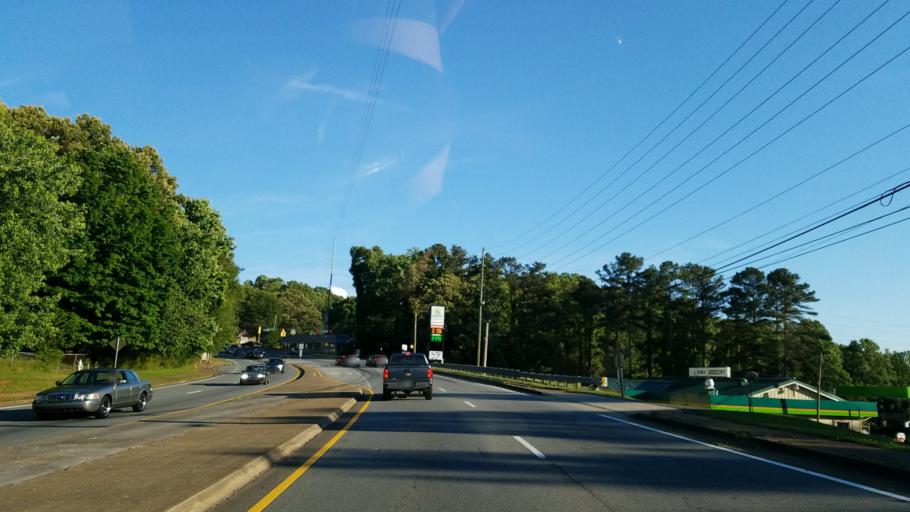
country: US
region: Georgia
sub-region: Cherokee County
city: Woodstock
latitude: 34.1210
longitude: -84.5860
